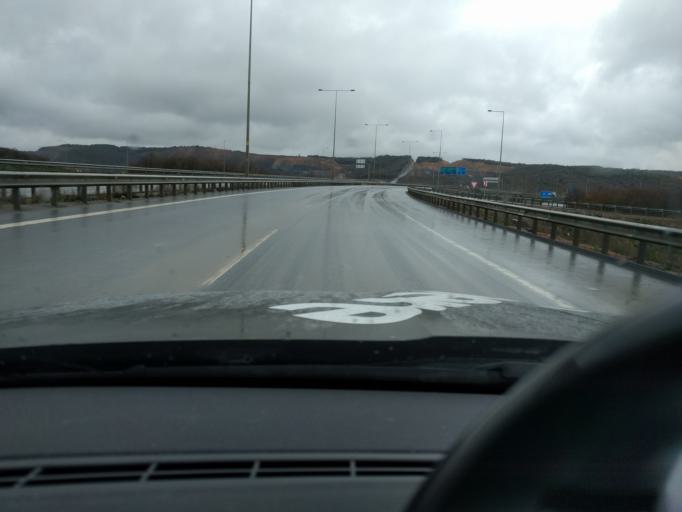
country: TR
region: Istanbul
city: Kemerburgaz
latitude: 41.2146
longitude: 28.8412
